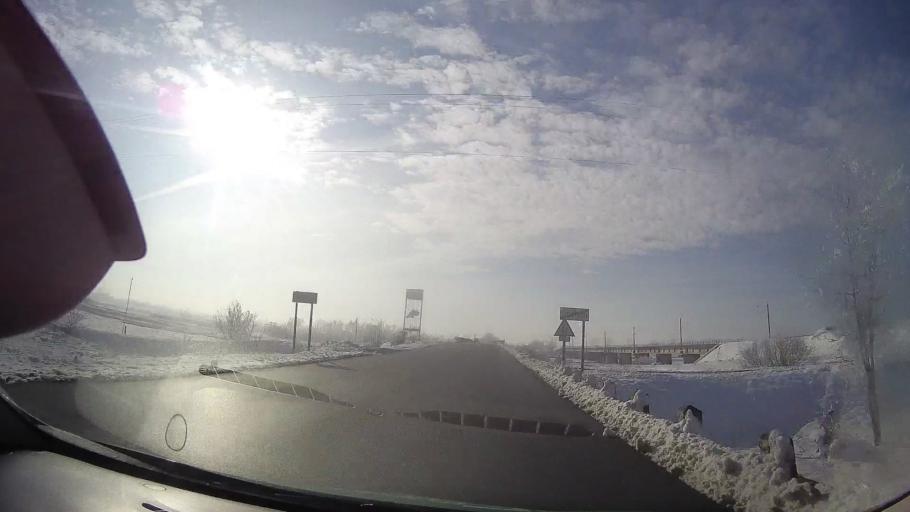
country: RO
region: Neamt
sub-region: Comuna Timisesti
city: Timisesti
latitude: 47.2482
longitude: 26.5465
